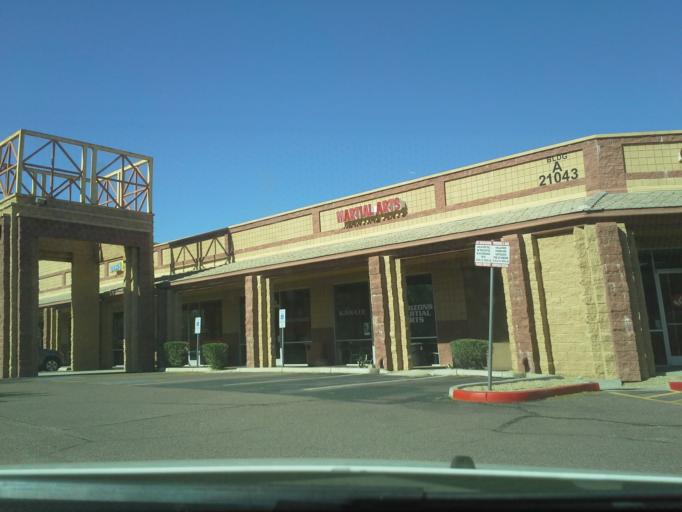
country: US
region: Arizona
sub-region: Maricopa County
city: Paradise Valley
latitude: 33.6783
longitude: -112.0294
